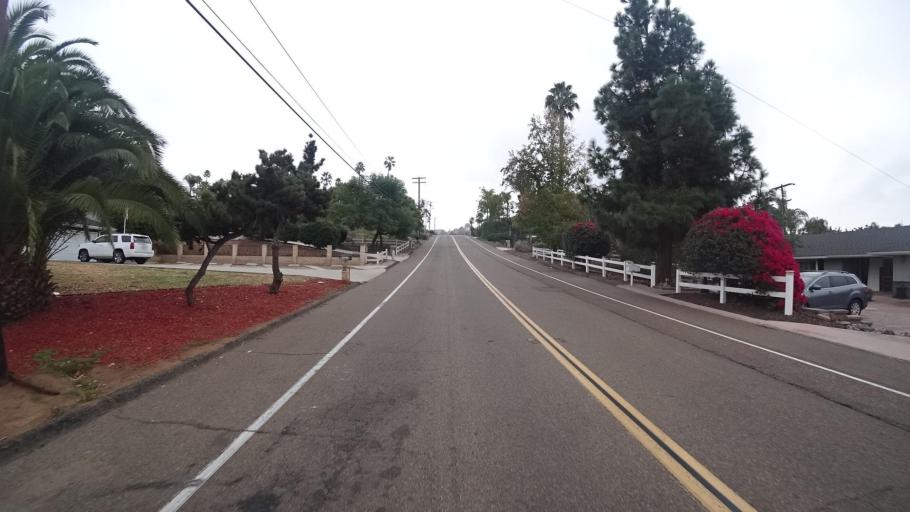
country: US
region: California
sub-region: San Diego County
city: Rancho San Diego
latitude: 32.7714
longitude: -116.9257
